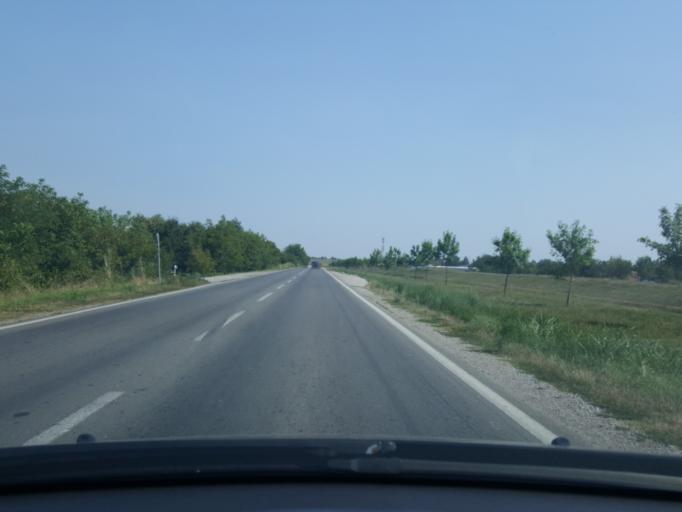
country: RS
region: Central Serbia
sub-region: Macvanski Okrug
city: Sabac
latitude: 44.7448
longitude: 19.6685
